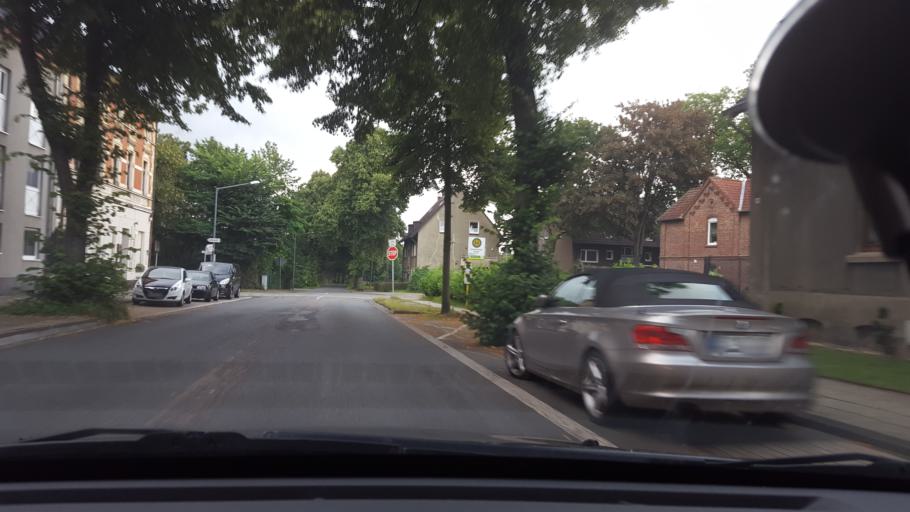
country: DE
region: North Rhine-Westphalia
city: Herten
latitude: 51.6244
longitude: 7.1420
